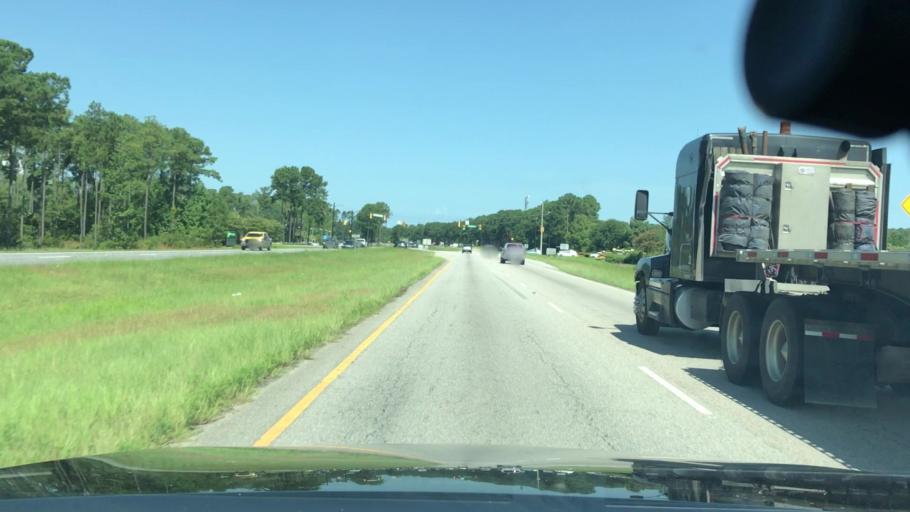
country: US
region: South Carolina
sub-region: Jasper County
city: Hardeeville
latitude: 32.3069
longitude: -80.9745
